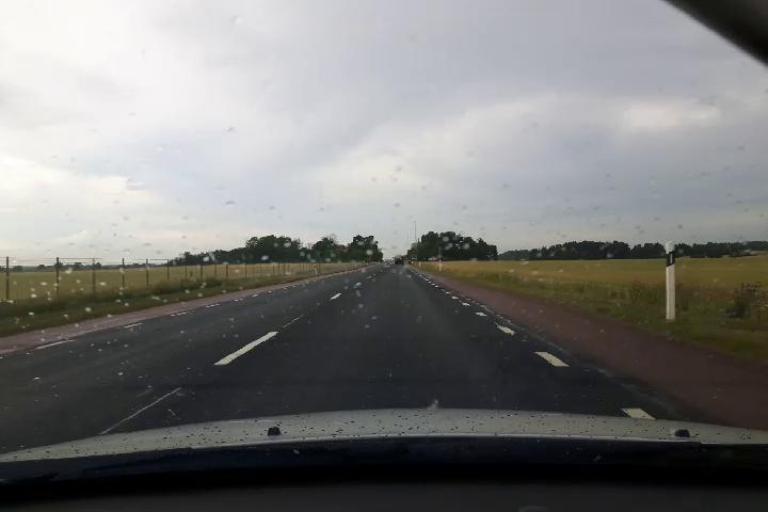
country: SE
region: Uppsala
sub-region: Uppsala Kommun
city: Gamla Uppsala
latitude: 59.9551
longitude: 17.5861
